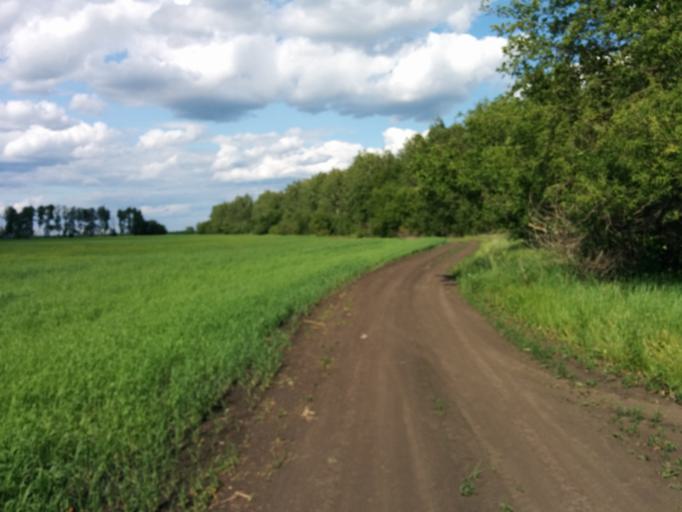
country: RU
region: Tambov
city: Tambov
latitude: 52.8026
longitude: 41.3881
